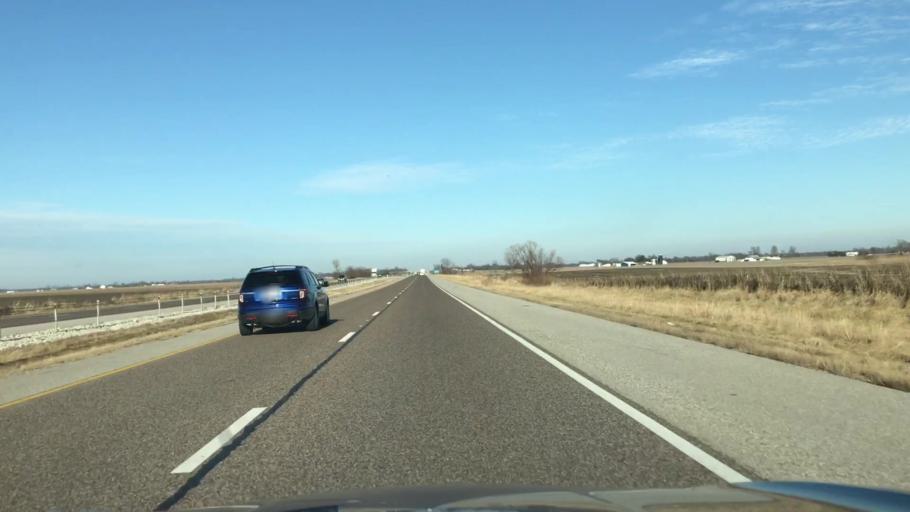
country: US
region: Illinois
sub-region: Madison County
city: Edwardsville
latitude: 38.8428
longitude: -89.8704
